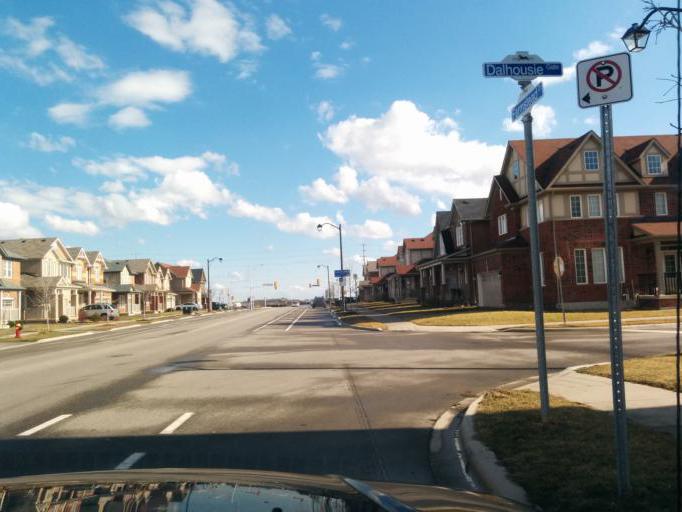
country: CA
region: Ontario
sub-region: Halton
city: Milton
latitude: 43.4925
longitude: -79.8554
